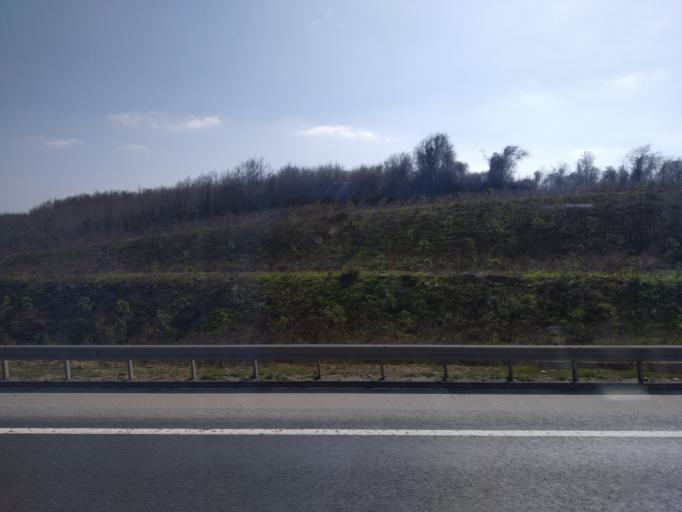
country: TR
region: Istanbul
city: Kemerburgaz
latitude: 41.2307
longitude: 28.8663
